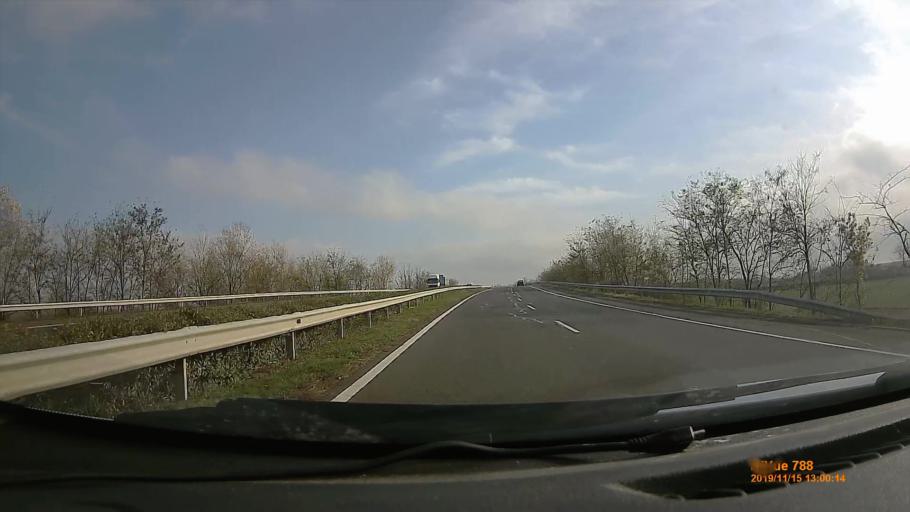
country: HU
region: Bekes
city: Gyula
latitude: 46.6613
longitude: 21.2041
